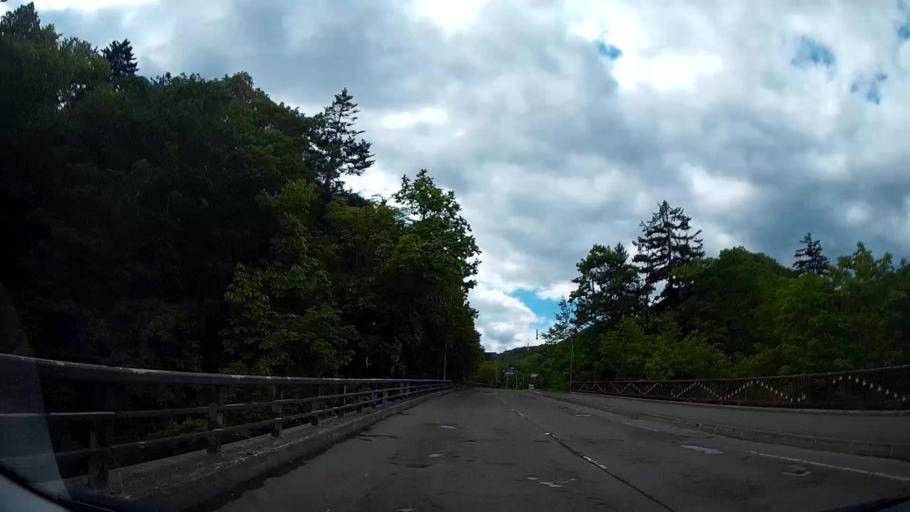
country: JP
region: Hokkaido
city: Kitahiroshima
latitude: 42.8645
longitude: 141.4093
